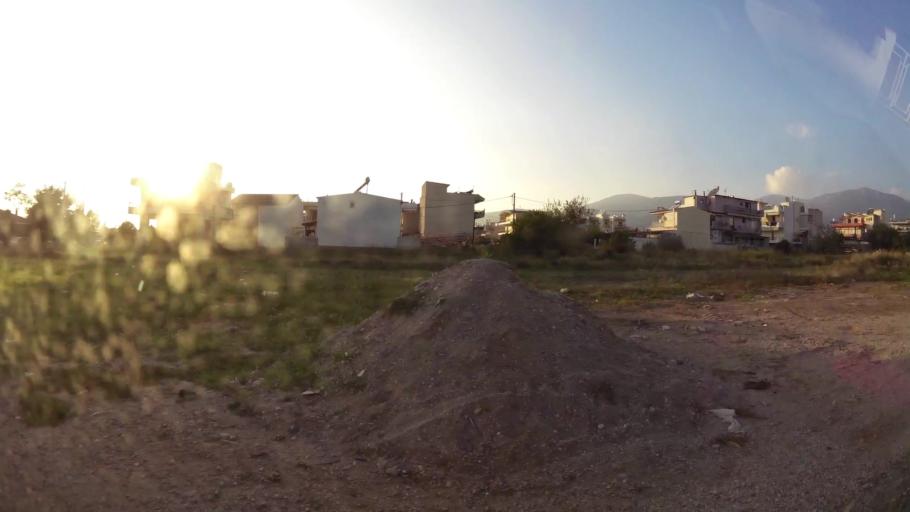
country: GR
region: Attica
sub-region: Nomarchia Anatolikis Attikis
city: Acharnes
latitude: 38.0948
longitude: 23.7442
